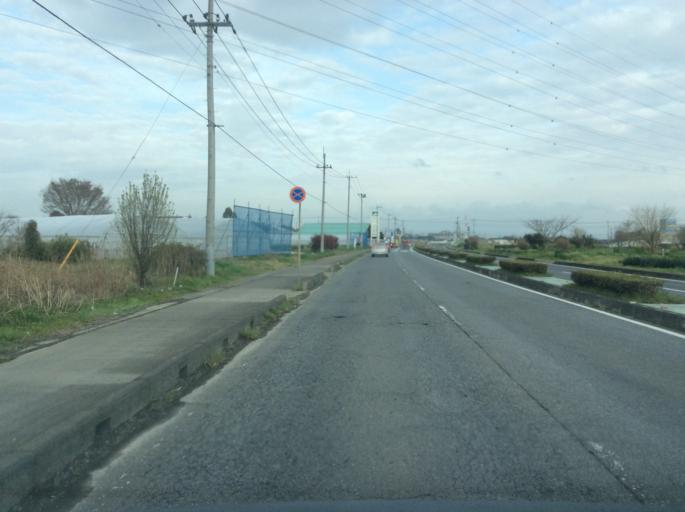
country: JP
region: Ibaraki
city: Naka
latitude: 36.1315
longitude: 140.1535
